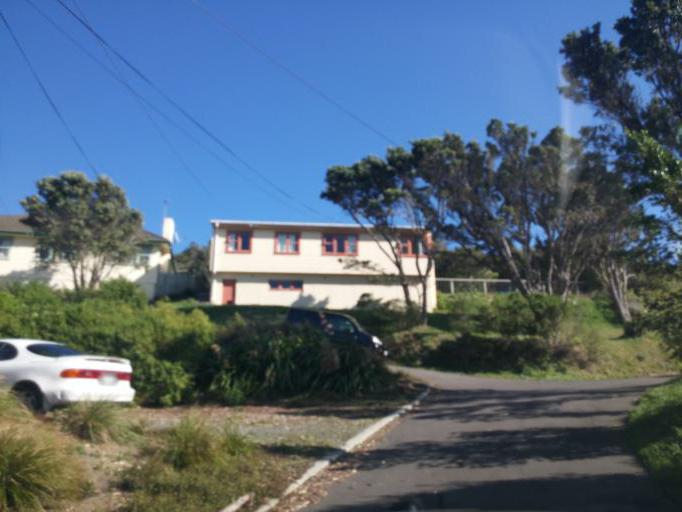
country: NZ
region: Wellington
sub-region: Wellington City
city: Wellington
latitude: -41.2527
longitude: 174.7856
